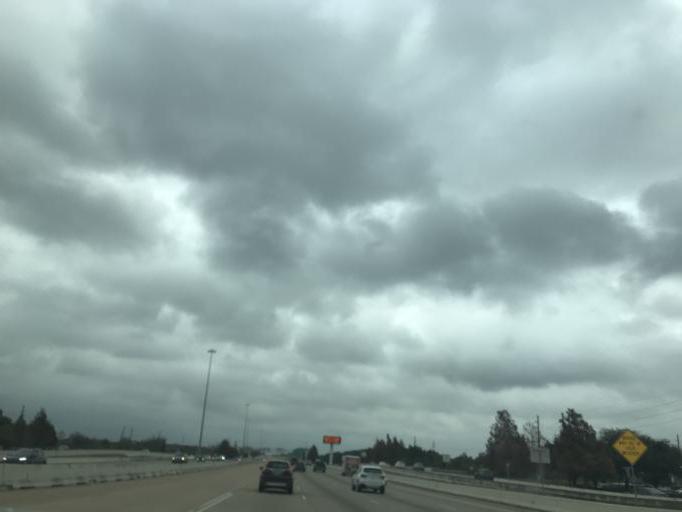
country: US
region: Texas
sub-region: Fort Bend County
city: Sugar Land
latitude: 29.6003
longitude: -95.6204
